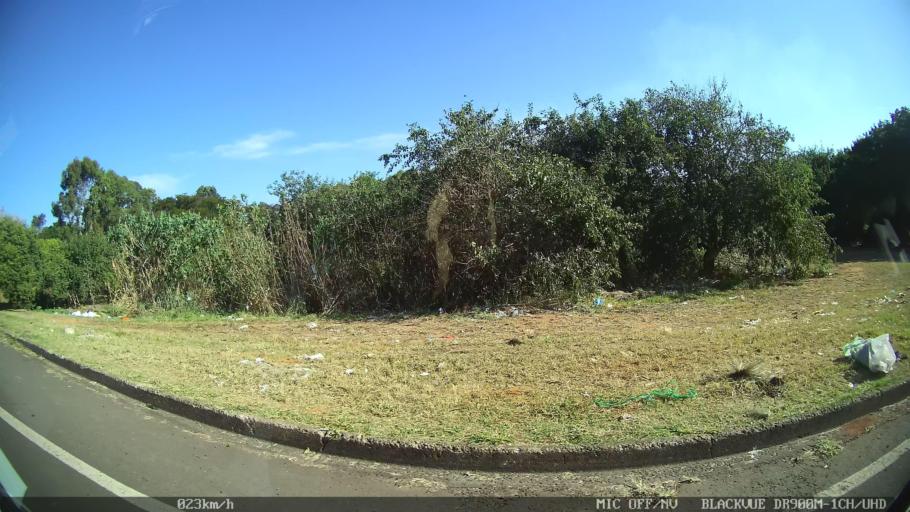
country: BR
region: Sao Paulo
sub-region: Franca
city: Franca
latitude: -20.5047
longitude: -47.4184
